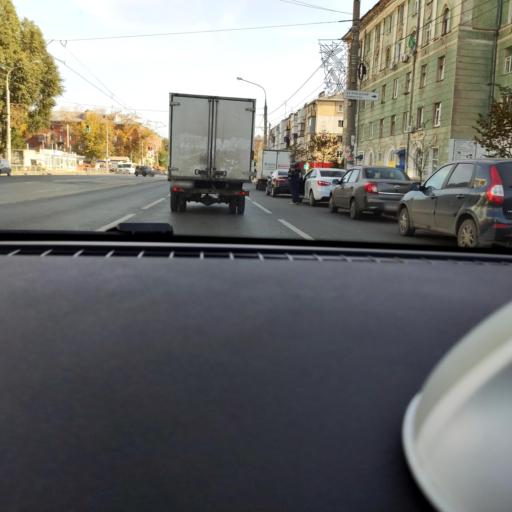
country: RU
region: Samara
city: Petra-Dubrava
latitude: 53.2252
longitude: 50.2755
